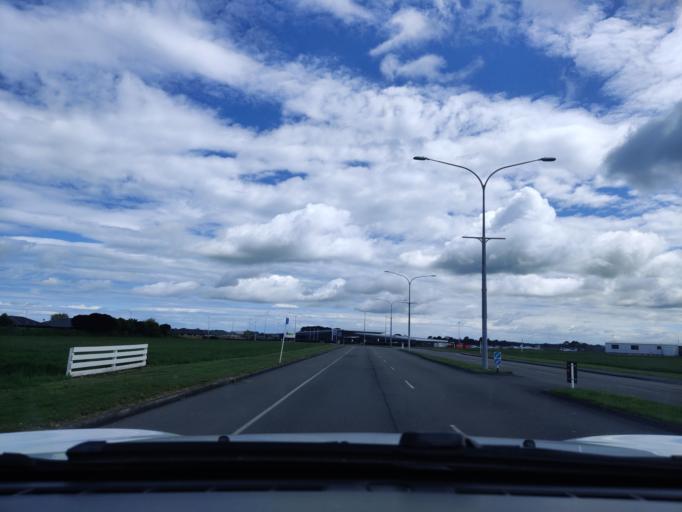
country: NZ
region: Manawatu-Wanganui
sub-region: Palmerston North City
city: Palmerston North
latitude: -40.3249
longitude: 175.6151
